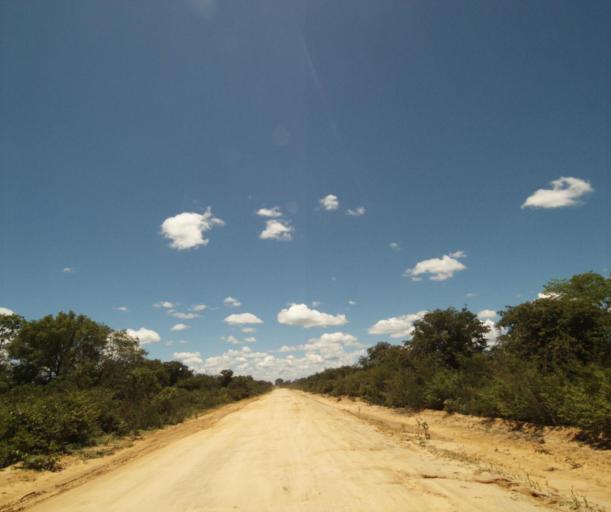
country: BR
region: Bahia
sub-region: Carinhanha
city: Carinhanha
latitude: -14.2254
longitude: -43.8722
